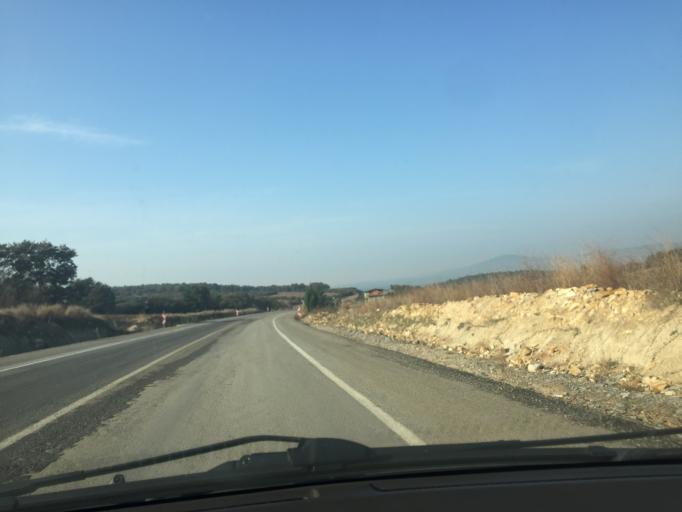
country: TR
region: Canakkale
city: Yigitler
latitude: 39.8894
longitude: 26.7110
